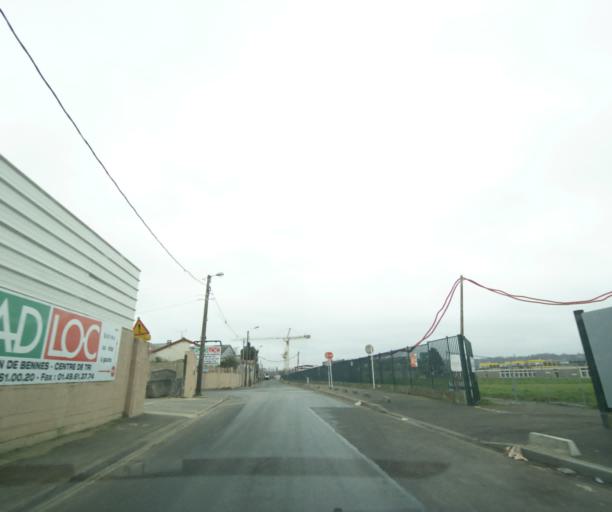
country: FR
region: Ile-de-France
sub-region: Departement du Val-de-Marne
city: Ablon-sur-Seine
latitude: 48.7317
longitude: 2.4284
